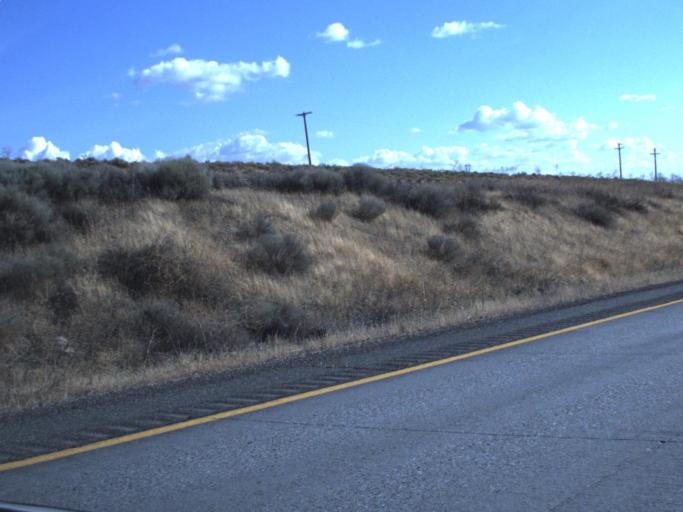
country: US
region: Washington
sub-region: Benton County
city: Highland
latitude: 46.0574
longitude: -119.2242
